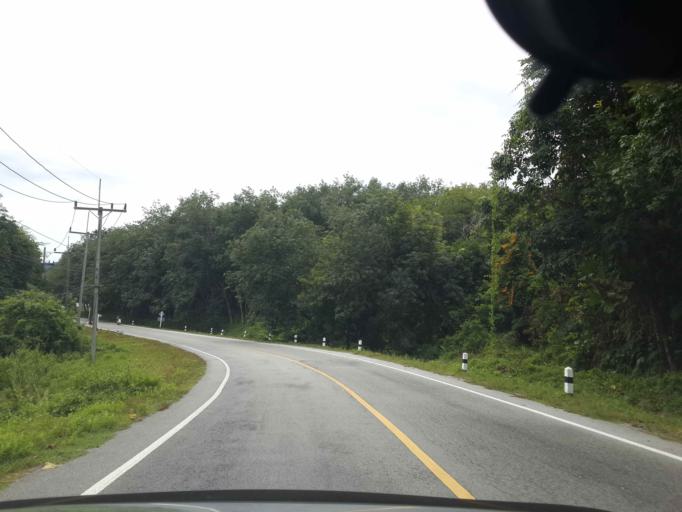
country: TH
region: Narathiwat
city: Rueso
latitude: 6.3601
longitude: 101.5562
